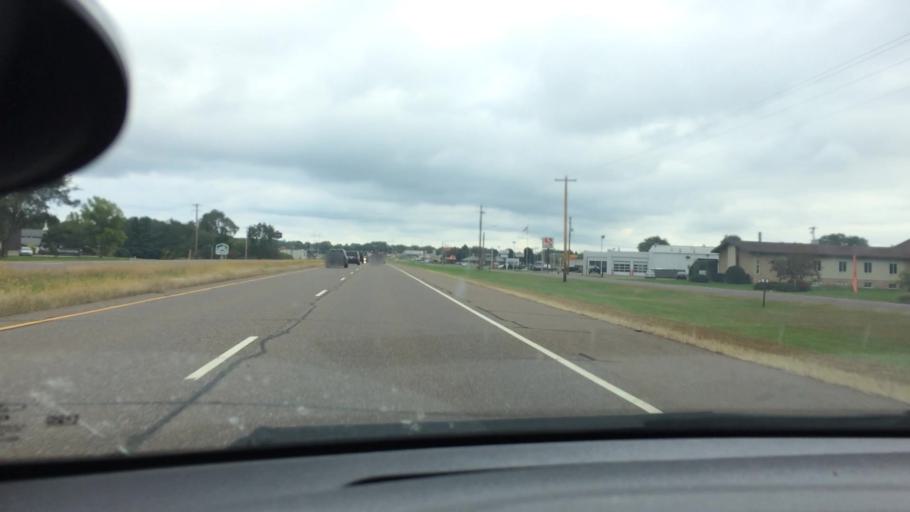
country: US
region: Wisconsin
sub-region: Chippewa County
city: Chippewa Falls
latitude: 44.9126
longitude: -91.3953
